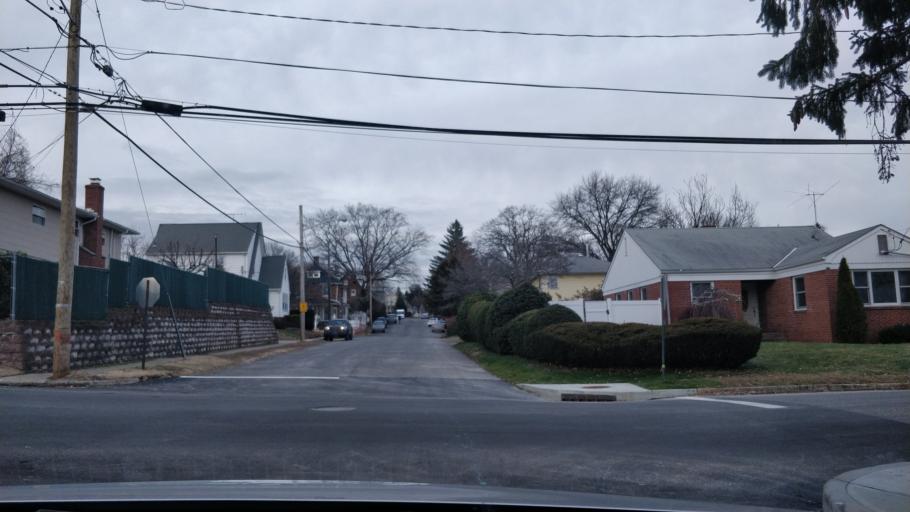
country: US
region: New York
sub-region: Nassau County
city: Glen Cove
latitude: 40.8645
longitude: -73.6413
